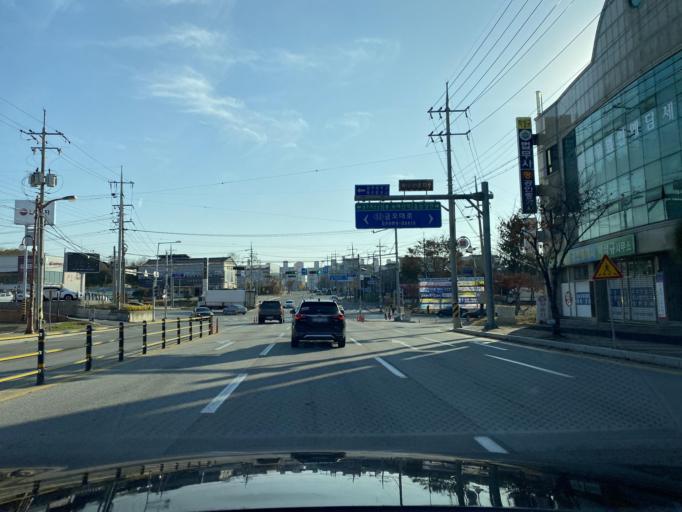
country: KR
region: Chungcheongnam-do
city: Yesan
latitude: 36.6933
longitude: 126.8364
